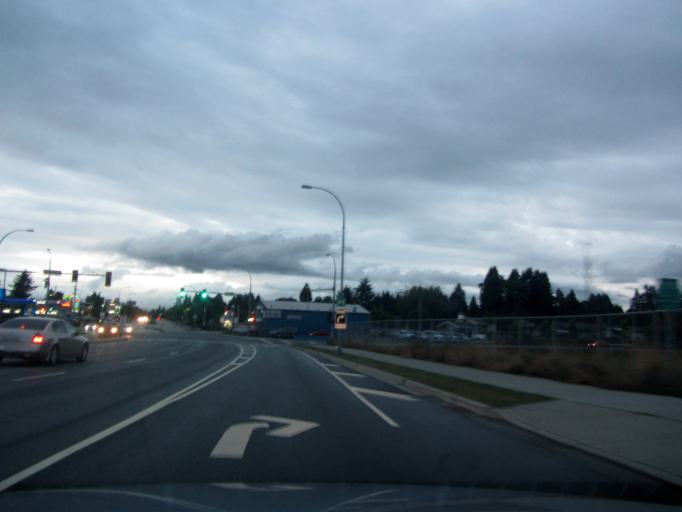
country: US
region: Washington
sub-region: Whatcom County
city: Sumas
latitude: 49.0387
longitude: -122.3373
